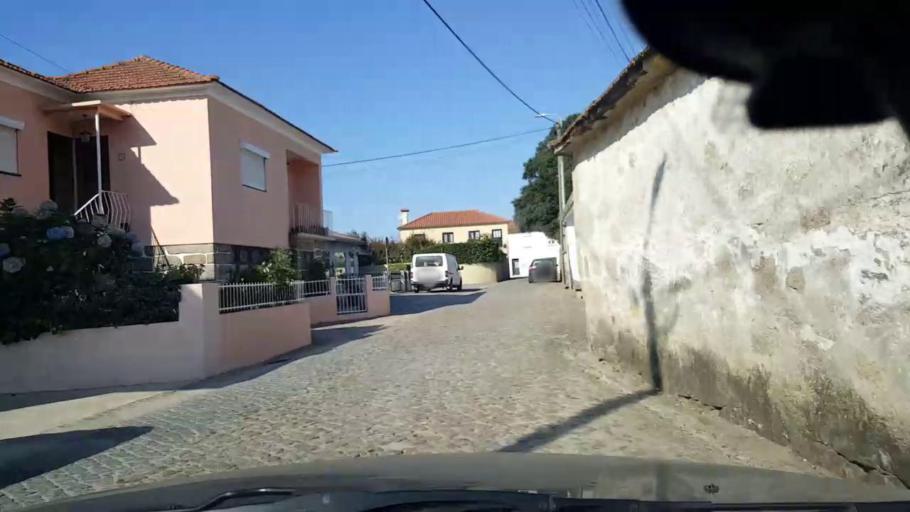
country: PT
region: Porto
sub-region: Vila do Conde
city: Arvore
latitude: 41.3562
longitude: -8.7182
